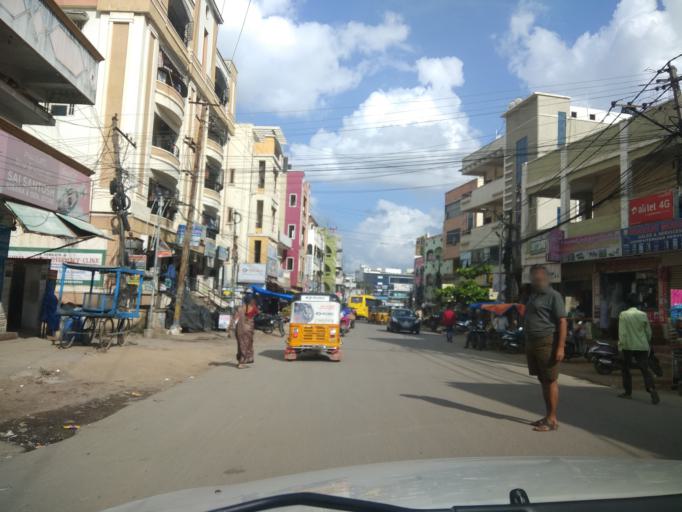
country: IN
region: Telangana
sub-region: Rangareddi
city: Kukatpalli
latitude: 17.4647
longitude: 78.3655
